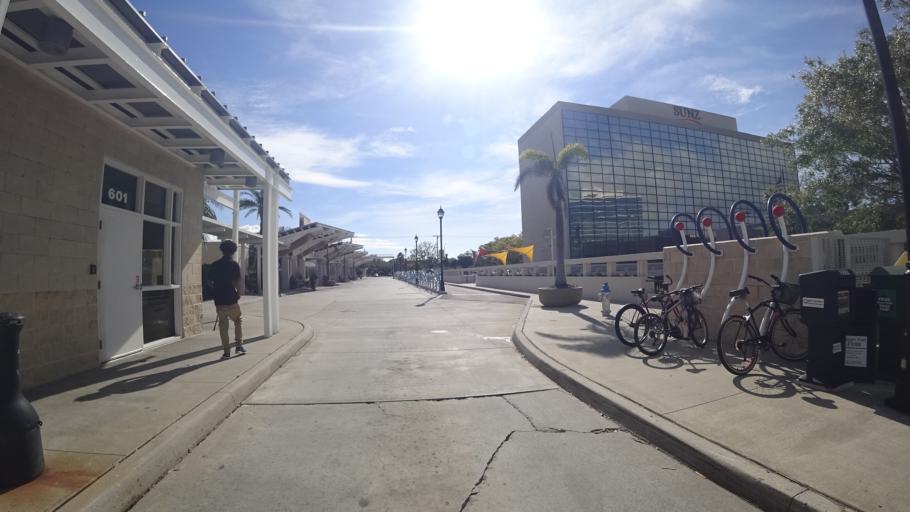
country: US
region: Florida
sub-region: Manatee County
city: Bradenton
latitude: 27.4941
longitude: -82.5743
